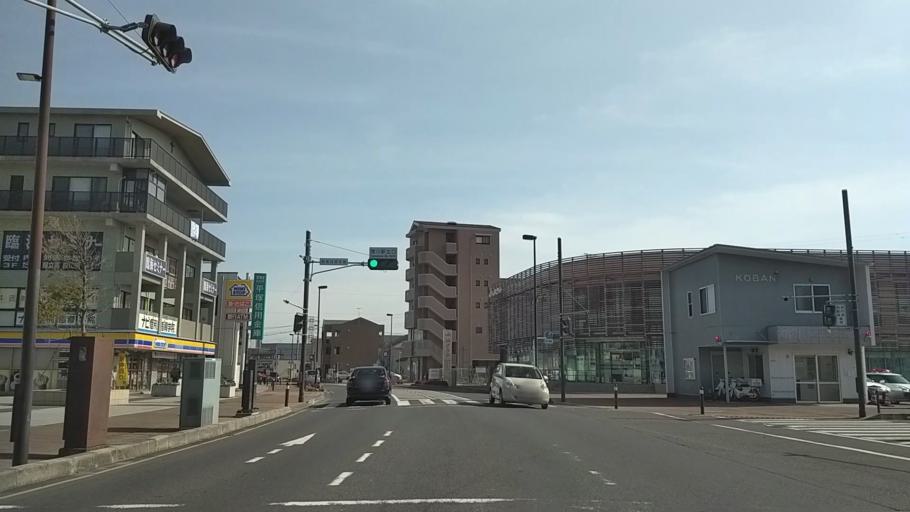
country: JP
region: Kanagawa
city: Chigasaki
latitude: 35.3686
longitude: 139.3874
